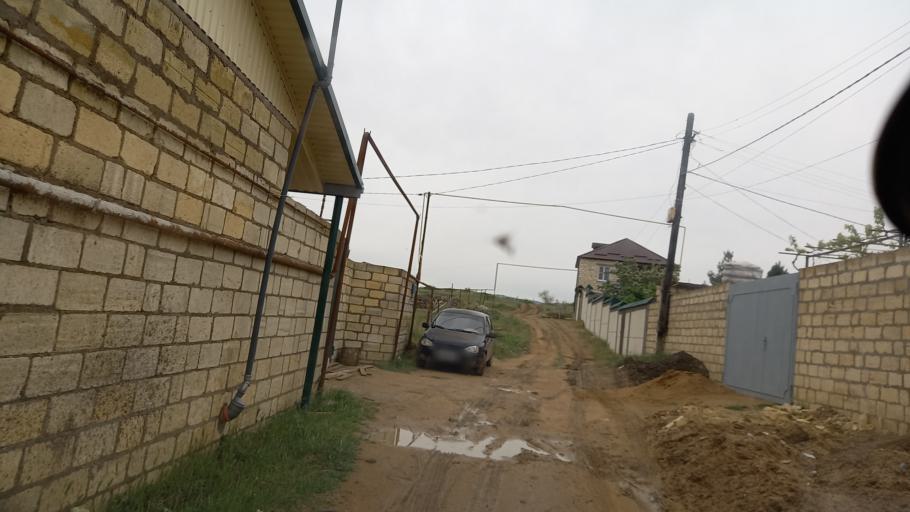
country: RU
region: Dagestan
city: Sabnova
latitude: 42.1183
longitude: 48.2649
